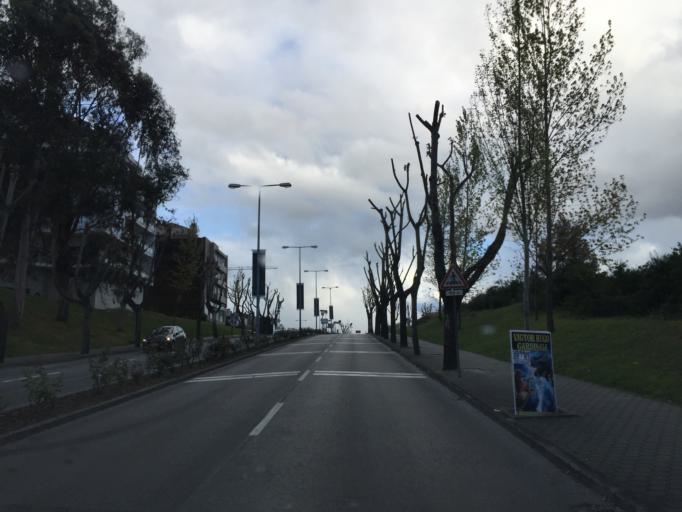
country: PT
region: Viseu
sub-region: Viseu
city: Viseu
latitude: 40.6575
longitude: -7.9232
